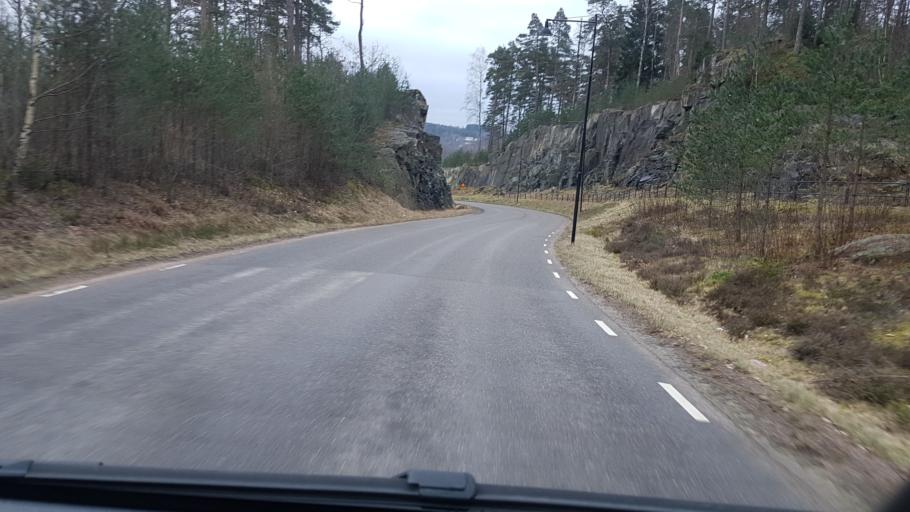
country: SE
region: Vaestra Goetaland
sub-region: Lerums Kommun
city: Lerum
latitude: 57.7830
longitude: 12.2783
